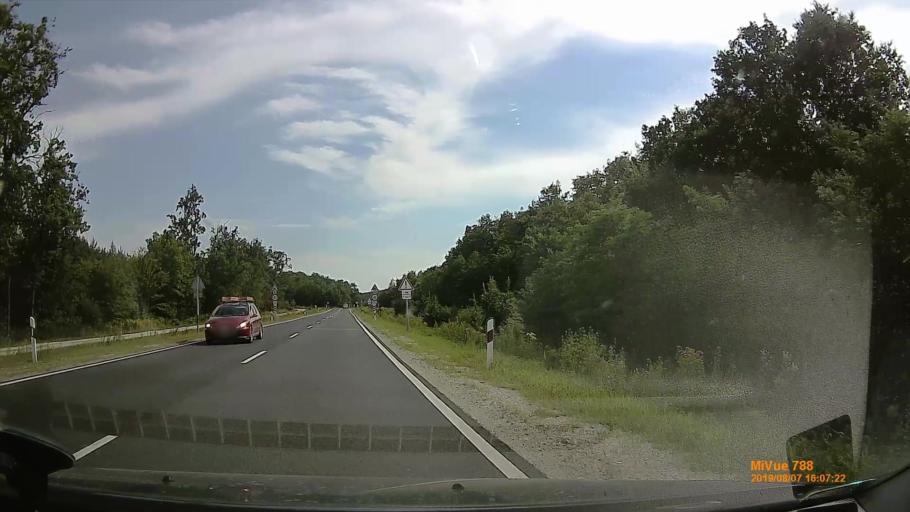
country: HU
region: Zala
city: Zalalovo
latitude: 46.9218
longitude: 16.5997
